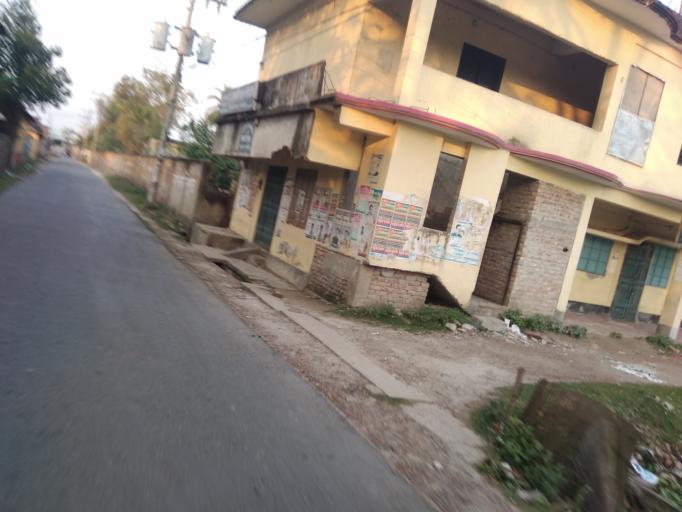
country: BD
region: Khulna
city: Satkhira
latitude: 22.5468
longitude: 89.1730
